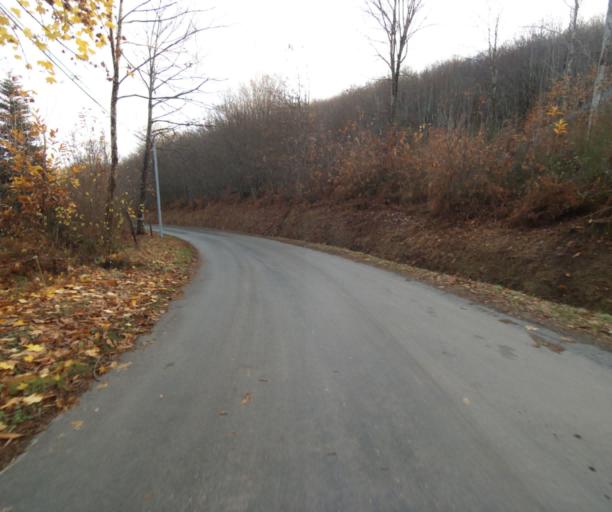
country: FR
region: Limousin
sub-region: Departement de la Correze
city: Sainte-Fortunade
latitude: 45.2087
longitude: 1.7546
